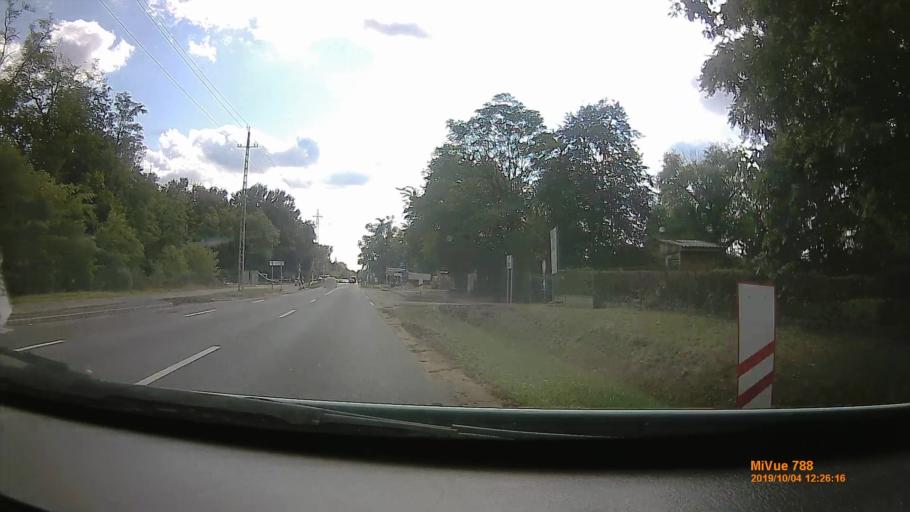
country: HU
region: Szabolcs-Szatmar-Bereg
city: Nyiregyhaza
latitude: 47.9776
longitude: 21.7054
